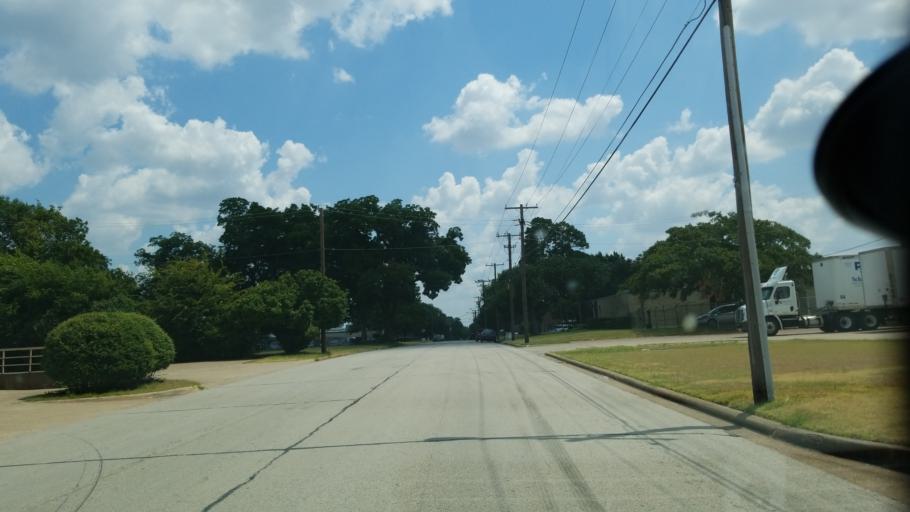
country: US
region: Texas
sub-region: Dallas County
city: Duncanville
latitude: 32.6896
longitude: -96.8887
